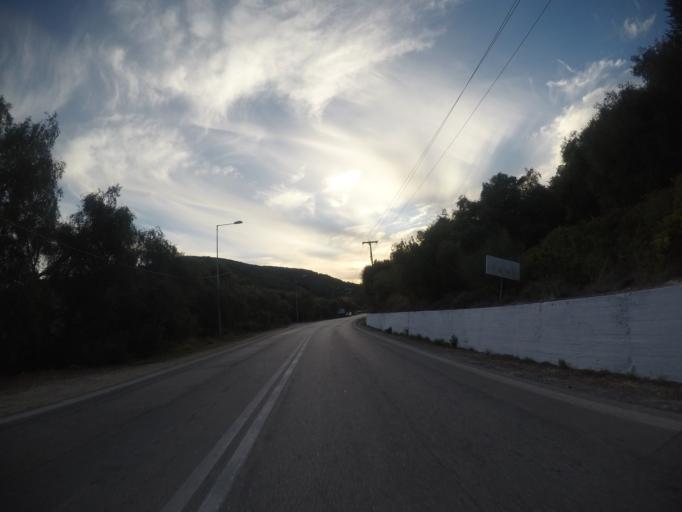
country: GR
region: Epirus
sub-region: Nomos Prevezis
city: Parga
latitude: 39.2854
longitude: 20.4301
